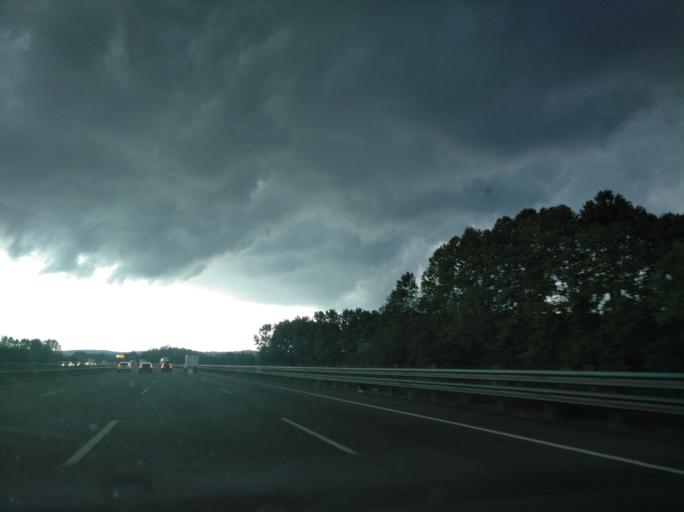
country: ES
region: Catalonia
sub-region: Provincia de Girona
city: Salt
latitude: 41.9804
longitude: 2.7800
